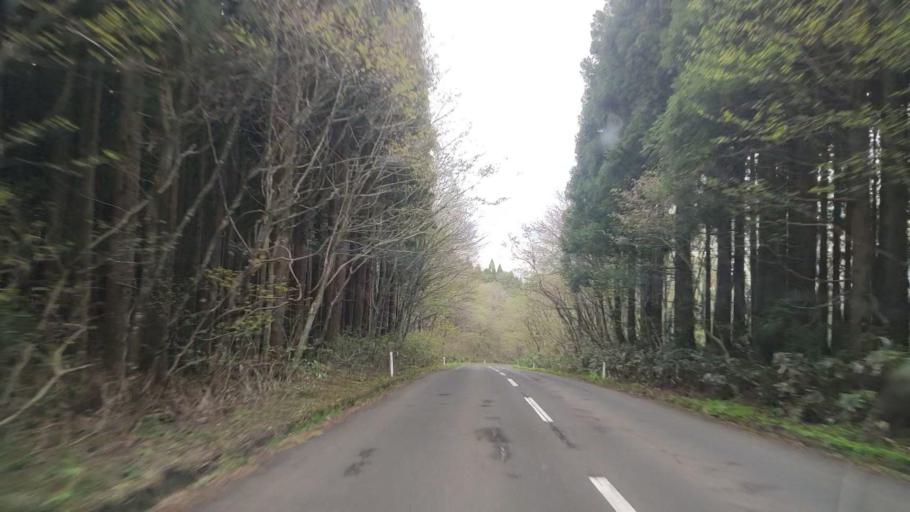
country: JP
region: Akita
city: Hanawa
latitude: 40.3854
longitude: 140.7926
